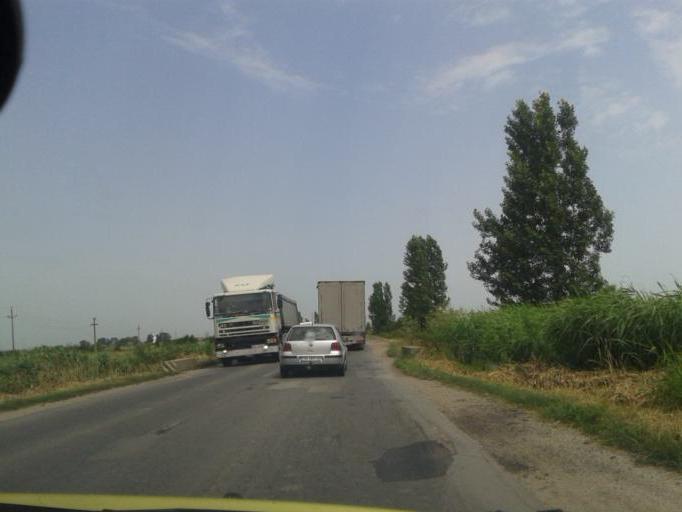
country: RO
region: Dambovita
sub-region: Oras Gaesti
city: Gaesti
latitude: 44.6935
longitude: 25.3124
